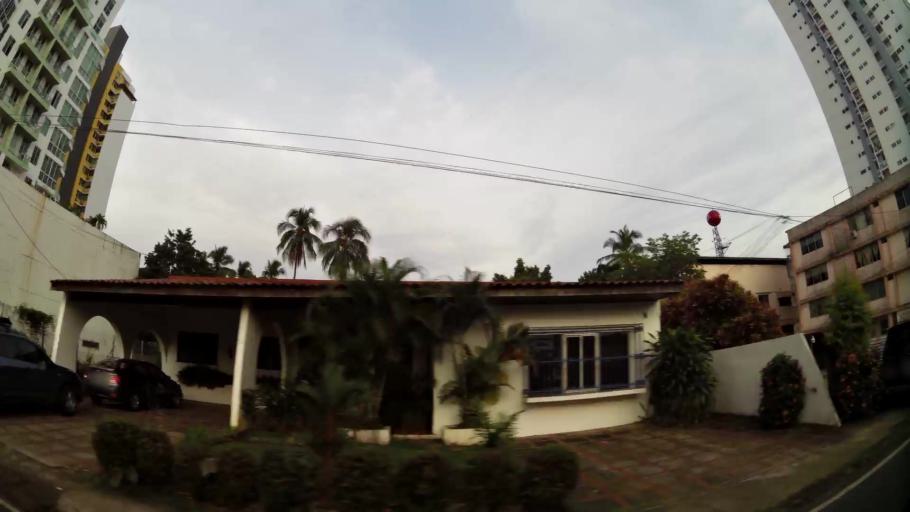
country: PA
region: Panama
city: Panama
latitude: 8.9927
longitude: -79.5116
